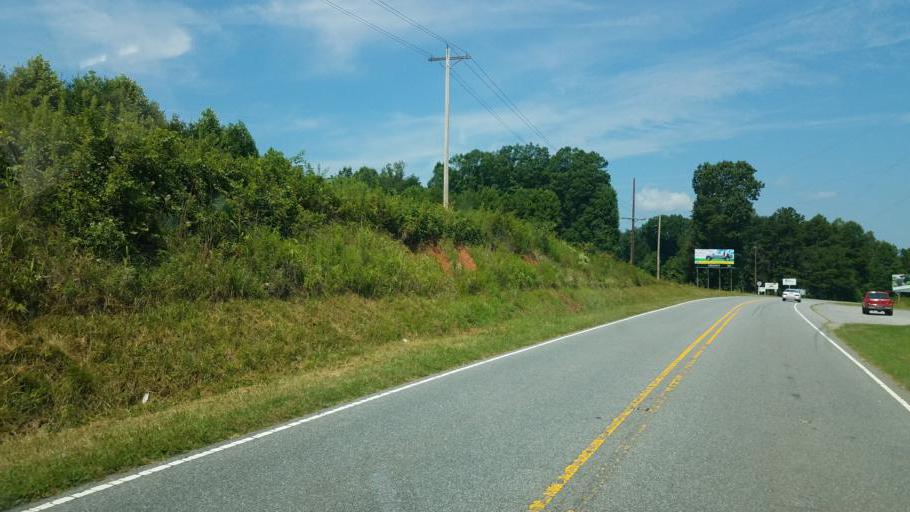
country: US
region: North Carolina
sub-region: Burke County
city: Icard
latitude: 35.5588
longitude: -81.5128
